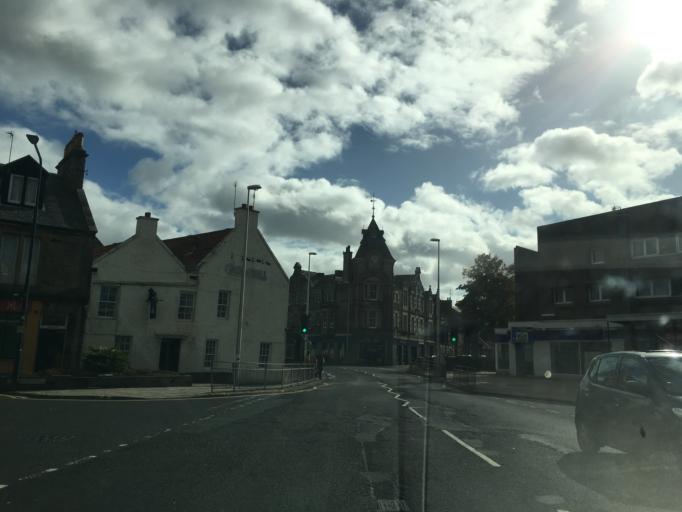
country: GB
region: Scotland
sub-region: Midlothian
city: Dalkeith
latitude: 55.8936
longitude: -3.0695
